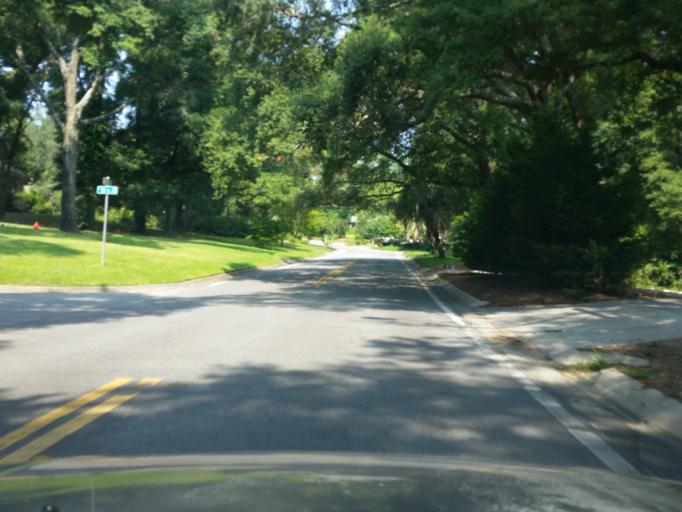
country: US
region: Florida
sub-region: Escambia County
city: Goulding
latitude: 30.4500
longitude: -87.2022
